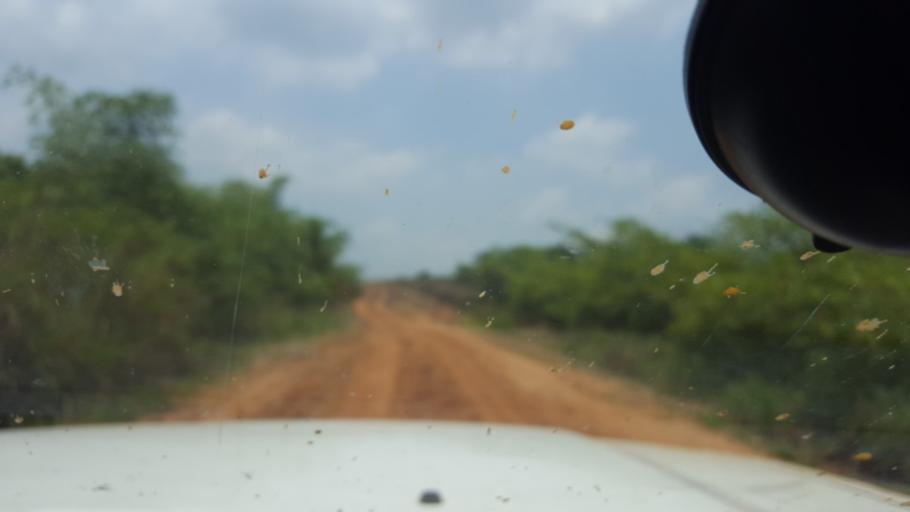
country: CD
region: Bandundu
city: Mushie
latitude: -3.7483
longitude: 16.6595
